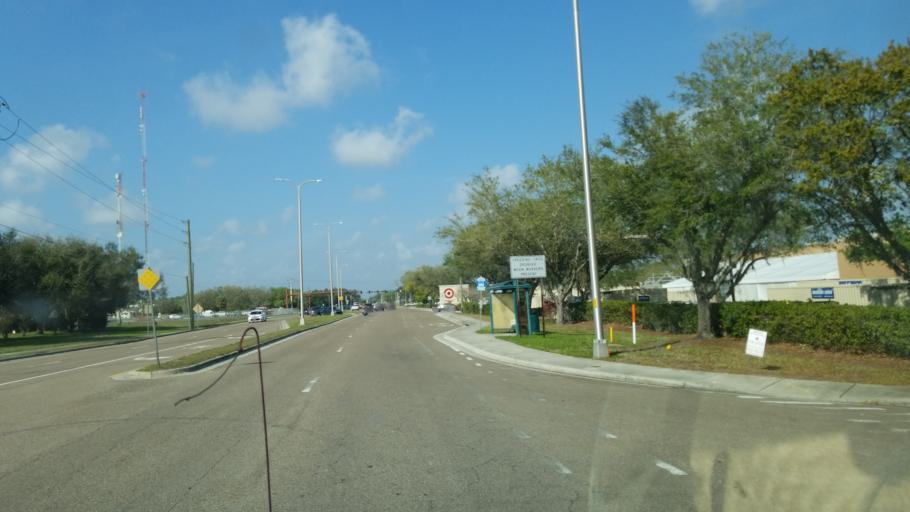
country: US
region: Florida
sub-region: Sarasota County
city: Fruitville
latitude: 27.3353
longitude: -82.4638
